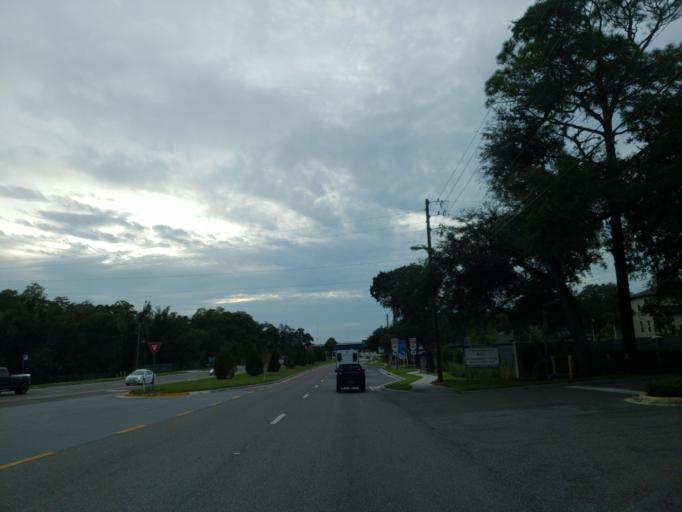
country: US
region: Florida
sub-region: Hillsborough County
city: Citrus Park
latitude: 28.0656
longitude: -82.5636
